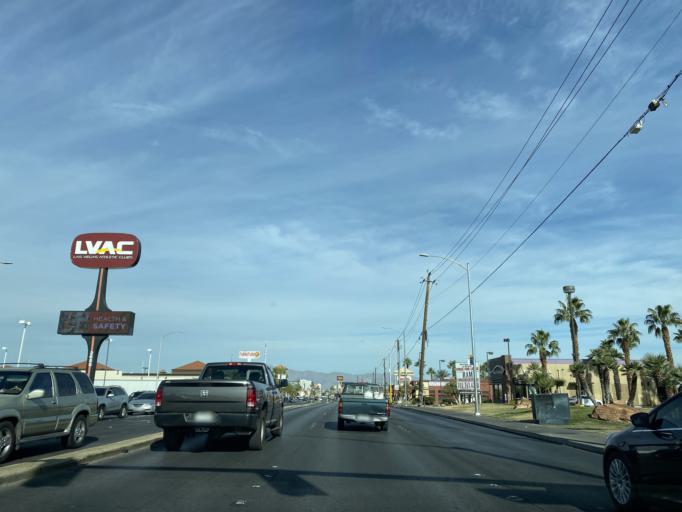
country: US
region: Nevada
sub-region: Clark County
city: Winchester
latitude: 36.1409
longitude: -115.1368
